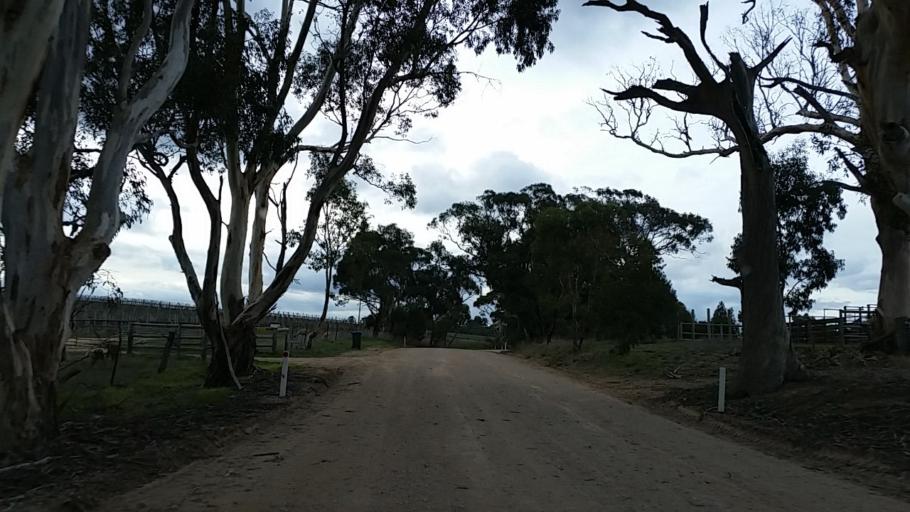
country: AU
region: South Australia
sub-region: Adelaide Hills
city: Woodside
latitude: -34.9440
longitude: 139.0126
